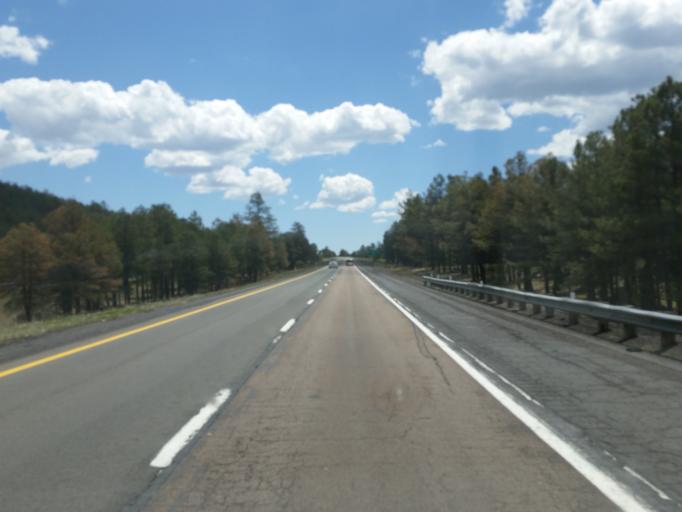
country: US
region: Arizona
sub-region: Coconino County
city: Flagstaff
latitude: 35.2015
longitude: -111.7612
